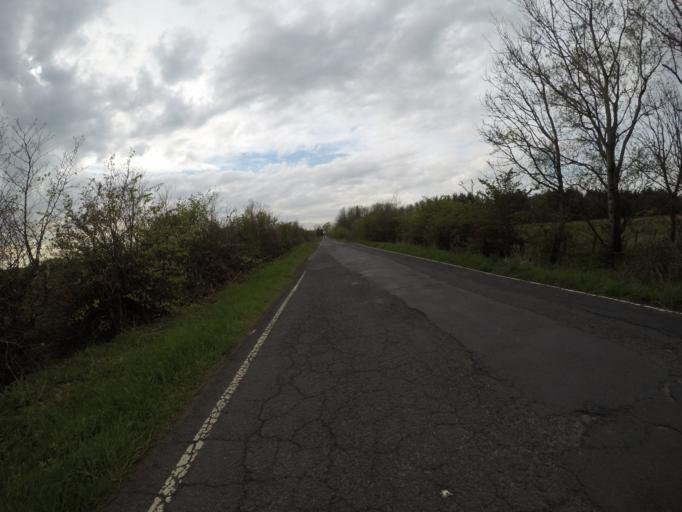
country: GB
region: Scotland
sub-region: East Ayrshire
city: Kilmarnock
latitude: 55.6435
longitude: -4.4808
